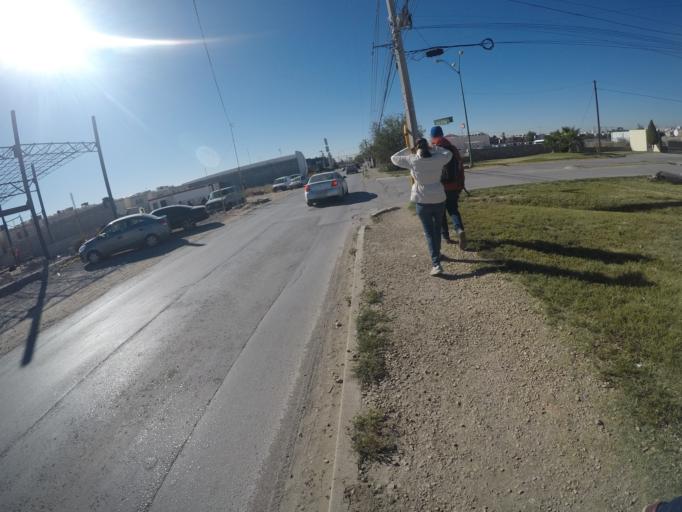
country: US
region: Texas
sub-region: El Paso County
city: Socorro
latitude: 31.6956
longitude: -106.3742
